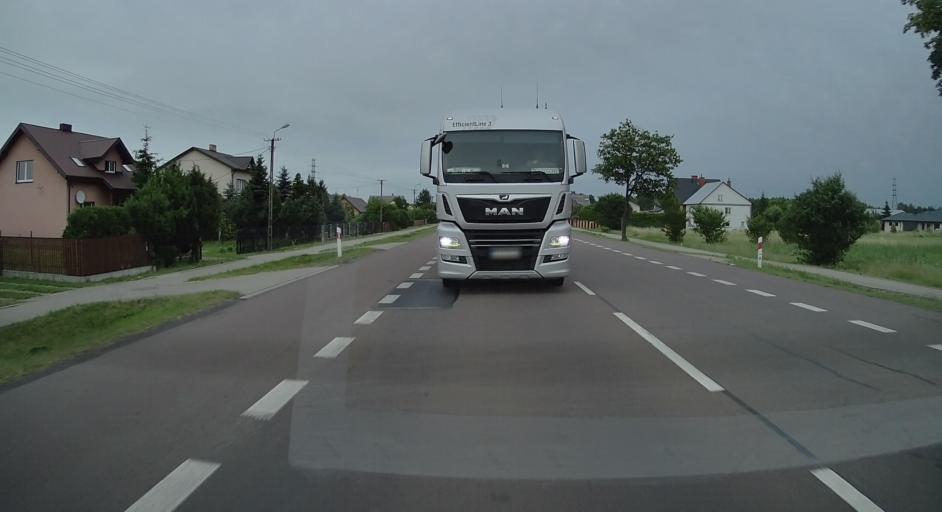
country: PL
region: Lublin Voivodeship
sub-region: Powiat bialski
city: Zalesie
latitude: 52.0373
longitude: 23.4768
